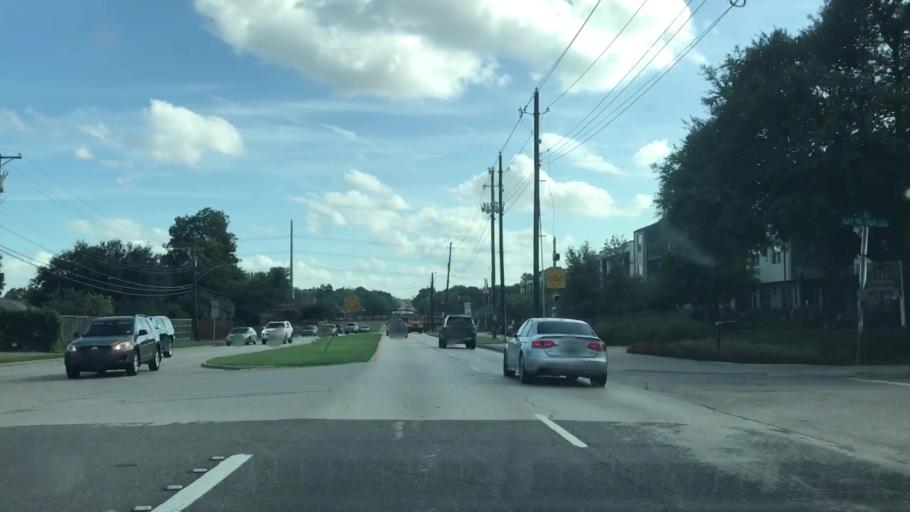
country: US
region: Texas
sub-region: Dallas County
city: Highland Park
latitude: 32.8444
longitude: -96.7615
